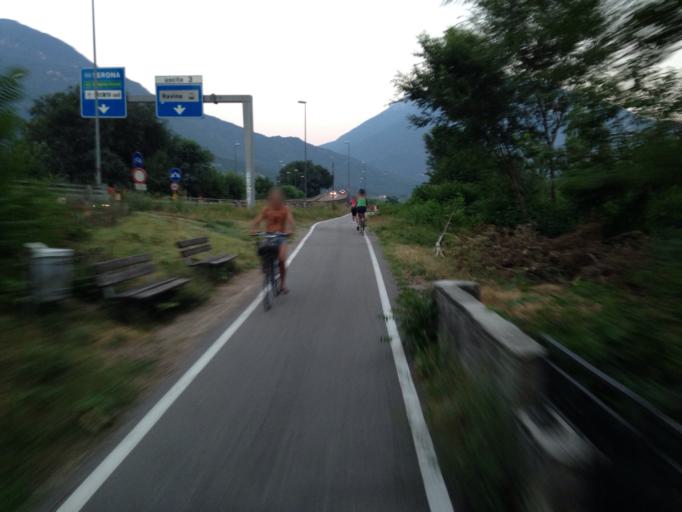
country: IT
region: Trentino-Alto Adige
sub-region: Provincia di Trento
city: Ravina
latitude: 46.0480
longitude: 11.1130
